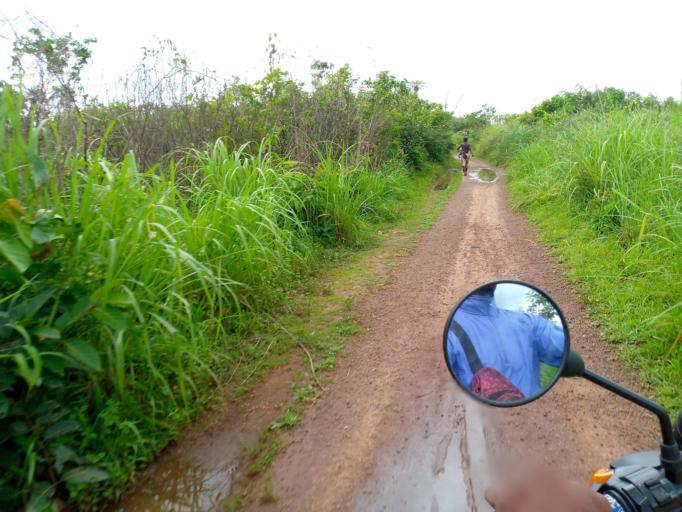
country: SL
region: Northern Province
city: Mange
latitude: 8.9824
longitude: -12.7322
